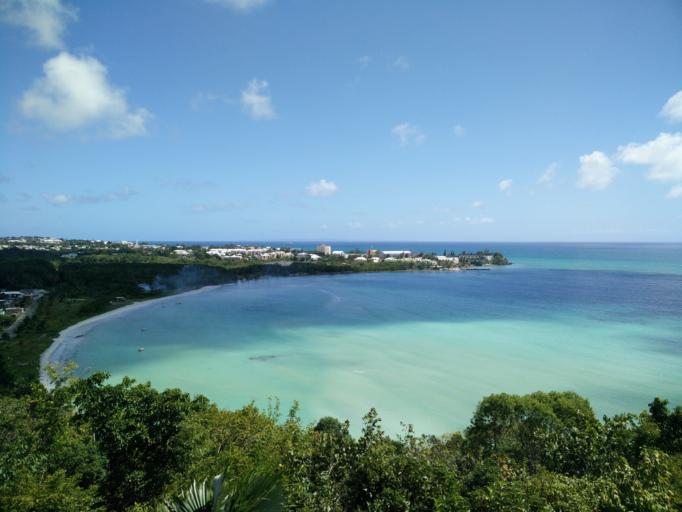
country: GP
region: Guadeloupe
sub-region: Guadeloupe
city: Le Gosier
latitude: 16.2170
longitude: -61.5126
